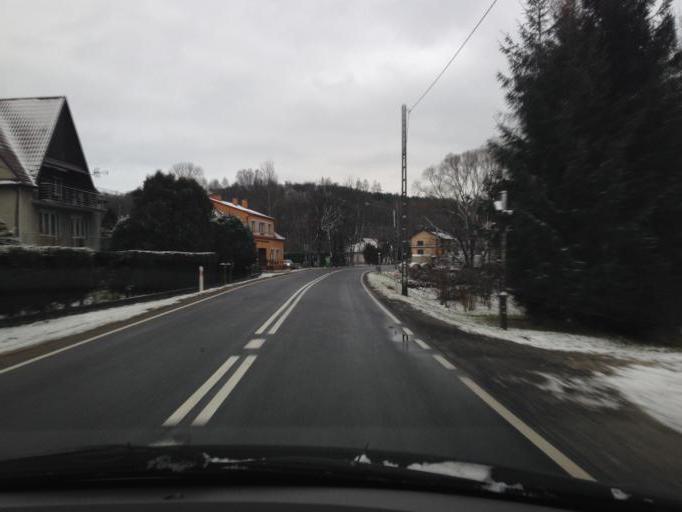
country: PL
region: Lesser Poland Voivodeship
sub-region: Powiat tarnowski
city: Siedliska
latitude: 49.8314
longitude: 21.0024
